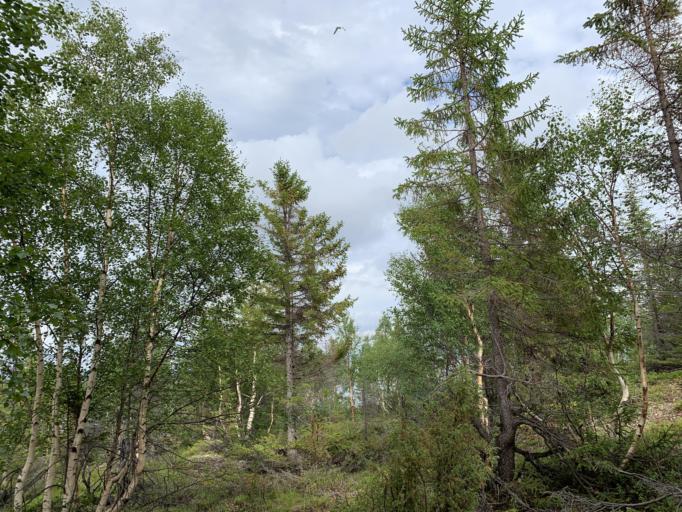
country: RU
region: Murmansk
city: Monchegorsk
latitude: 67.7968
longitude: 32.8134
